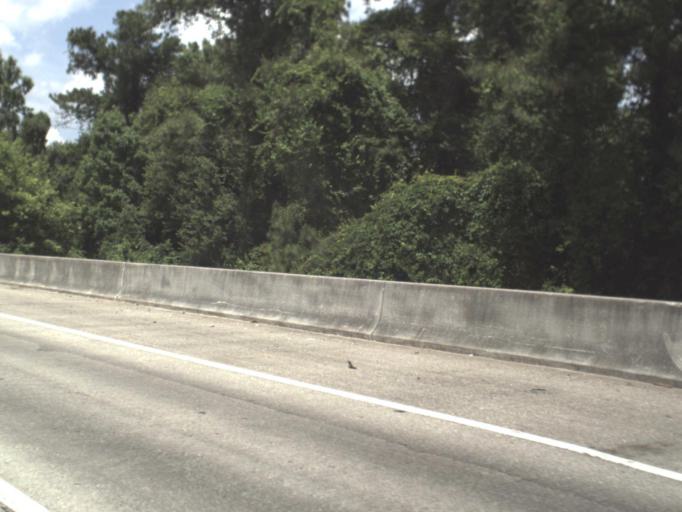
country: US
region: Florida
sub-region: Duval County
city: Jacksonville
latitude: 30.3053
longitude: -81.7701
